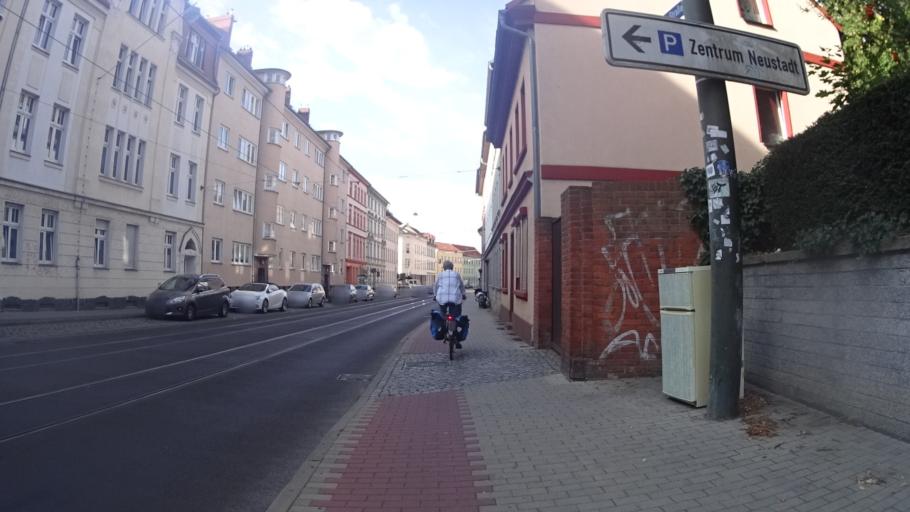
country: DE
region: Brandenburg
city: Brandenburg an der Havel
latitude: 52.4098
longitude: 12.5491
